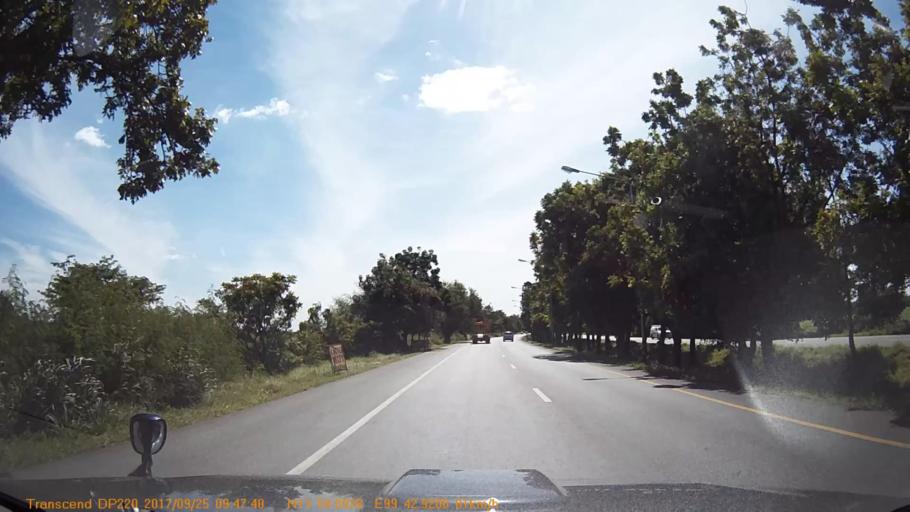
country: TH
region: Kanchanaburi
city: Tha Maka
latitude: 13.9681
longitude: 99.7158
